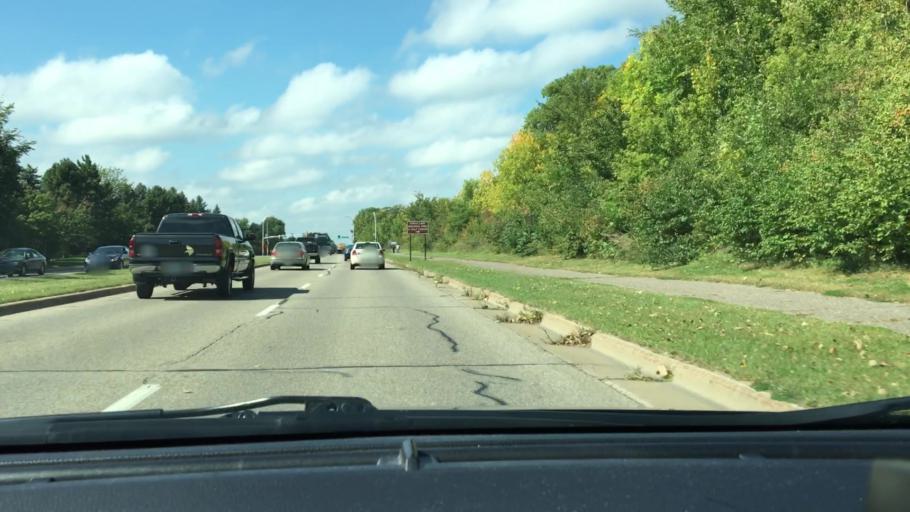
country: US
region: Minnesota
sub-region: Hennepin County
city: New Hope
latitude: 45.0587
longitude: -93.4173
